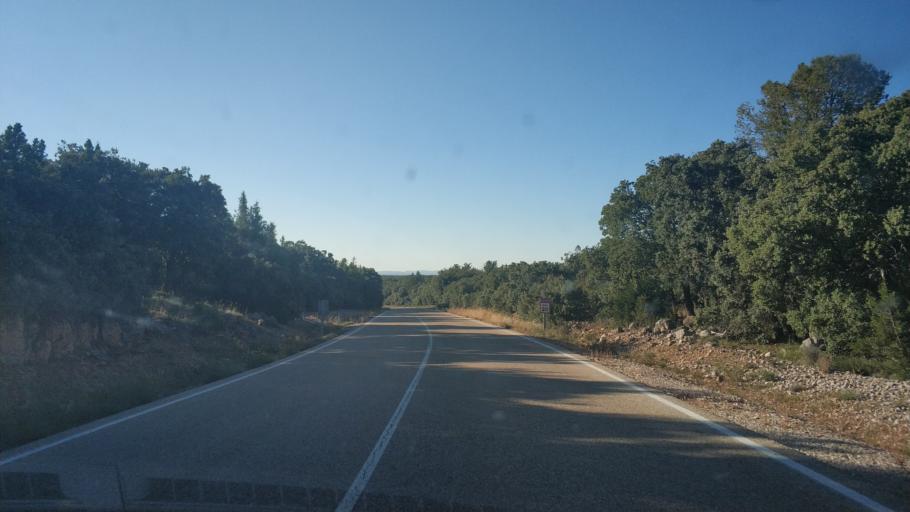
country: ES
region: Castille and Leon
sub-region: Provincia de Soria
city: Montejo de Tiermes
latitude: 41.4120
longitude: -3.2010
